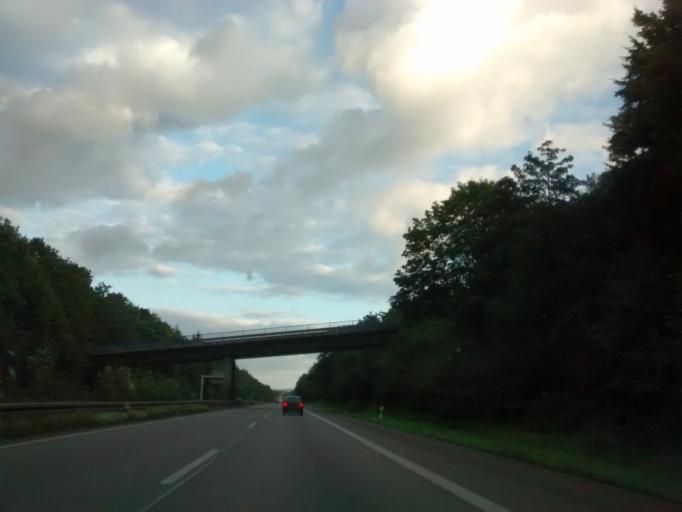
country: DE
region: North Rhine-Westphalia
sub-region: Regierungsbezirk Munster
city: Birgte
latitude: 52.2663
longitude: 7.6724
